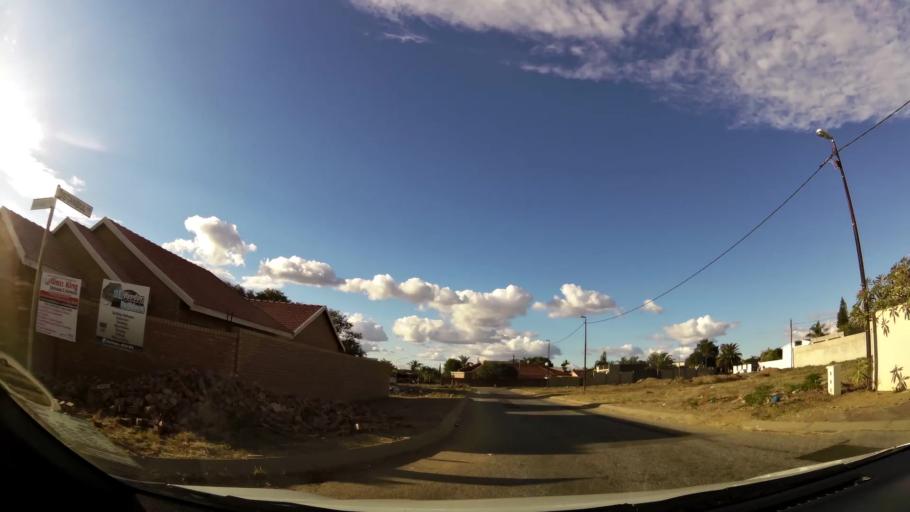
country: ZA
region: Limpopo
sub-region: Capricorn District Municipality
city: Polokwane
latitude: -23.9182
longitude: 29.4310
